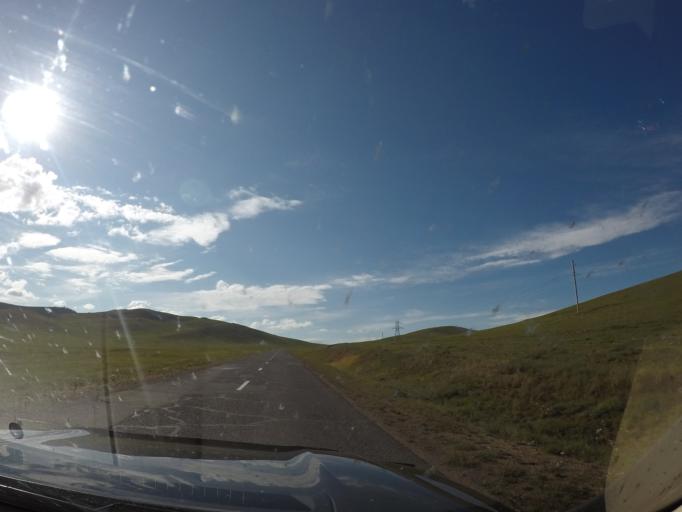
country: MN
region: Hentiy
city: Modot
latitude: 47.7714
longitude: 108.8649
